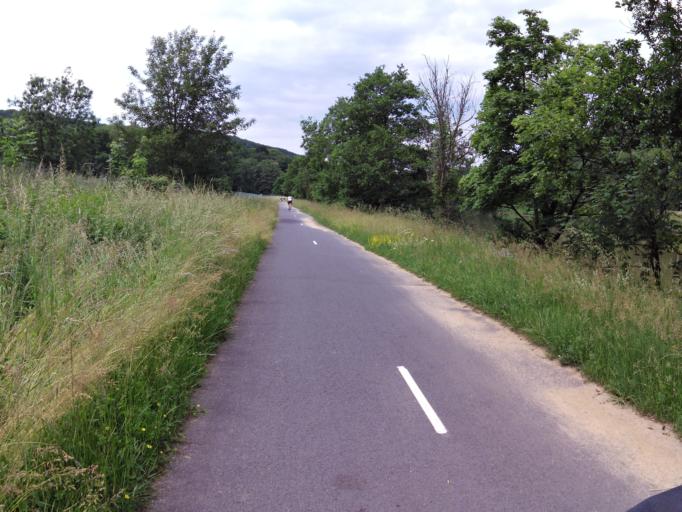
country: FR
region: Champagne-Ardenne
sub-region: Departement des Ardennes
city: Nouzonville
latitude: 49.8006
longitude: 4.7552
